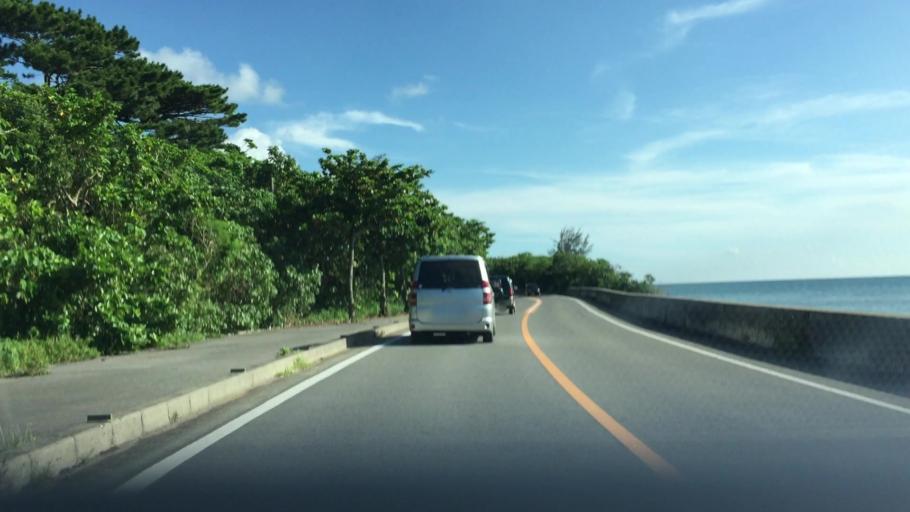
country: JP
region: Okinawa
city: Ishigaki
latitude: 24.4300
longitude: 124.1249
